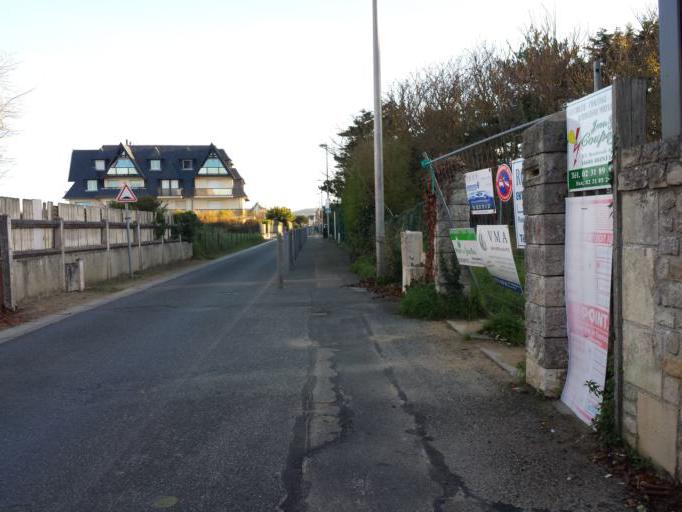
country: FR
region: Lower Normandy
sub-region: Departement du Calvados
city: Deauville
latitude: 49.3496
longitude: 0.0492
